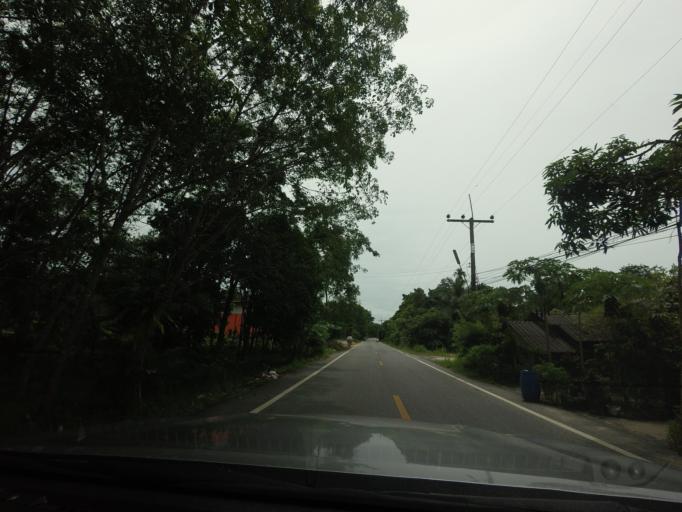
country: TH
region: Pattani
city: Kapho
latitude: 6.6216
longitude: 101.5439
